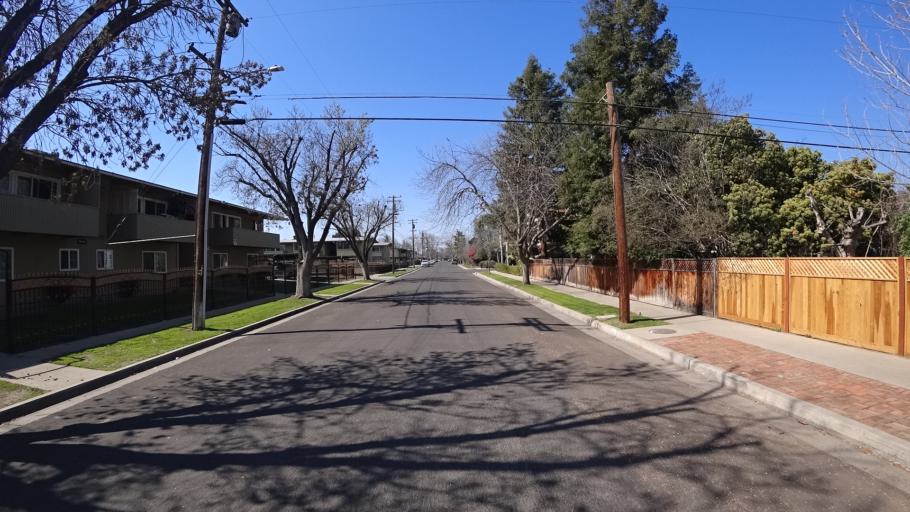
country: US
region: California
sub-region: Fresno County
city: Fresno
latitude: 36.7554
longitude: -119.7956
